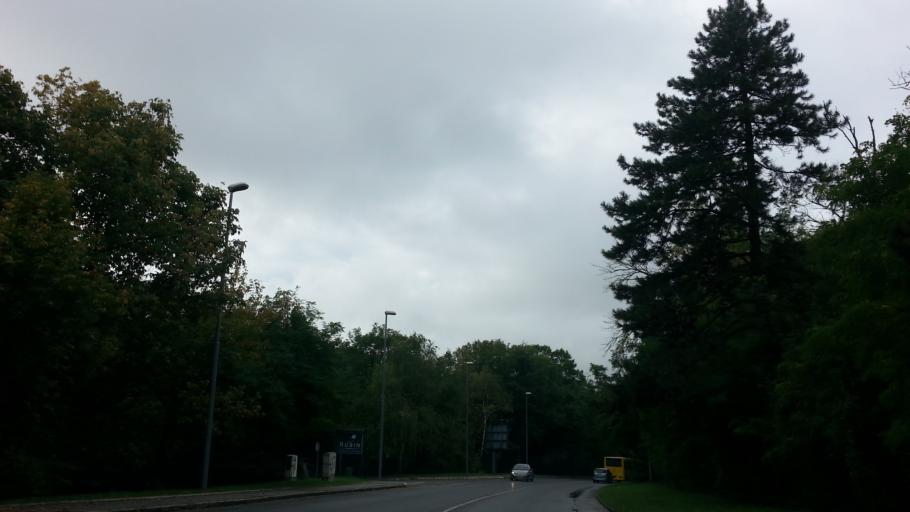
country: RS
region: Central Serbia
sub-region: Belgrade
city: Rakovica
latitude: 44.7542
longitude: 20.4374
